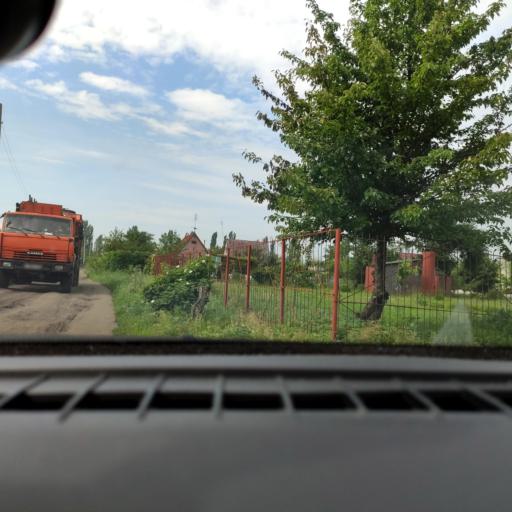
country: RU
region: Voronezj
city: Maslovka
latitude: 51.5035
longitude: 39.1996
